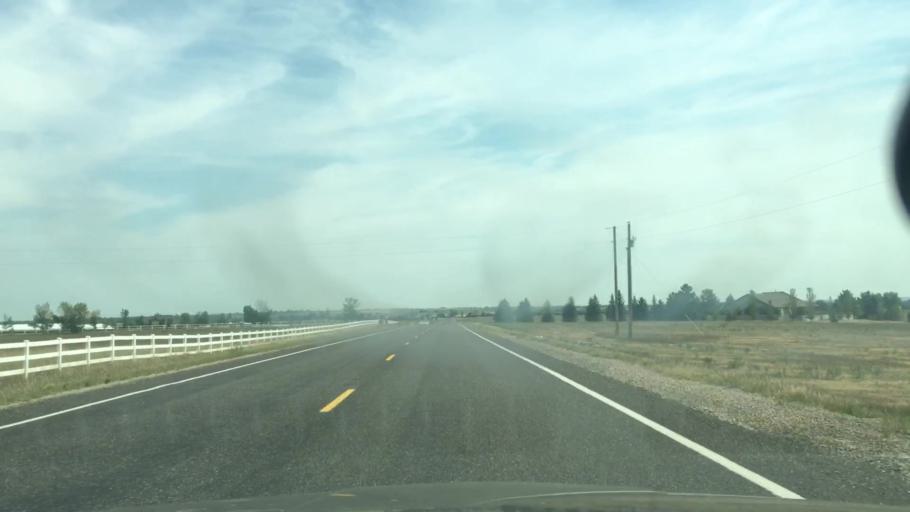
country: US
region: Colorado
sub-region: Larimer County
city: Berthoud
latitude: 40.3346
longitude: -105.1610
